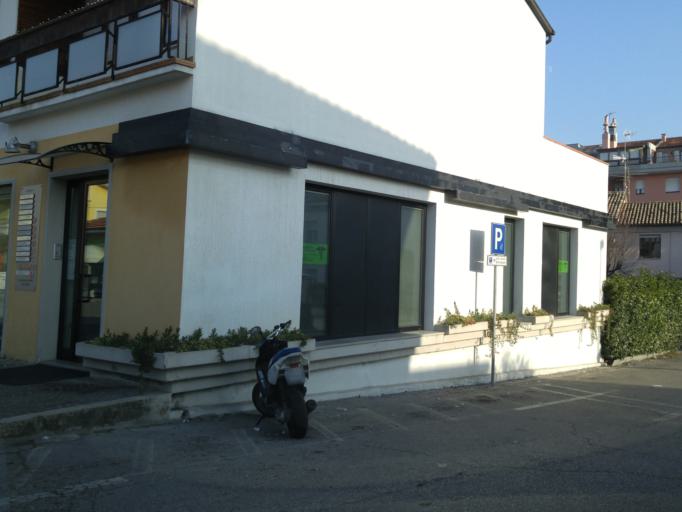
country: IT
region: The Marches
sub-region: Provincia di Pesaro e Urbino
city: Lucrezia
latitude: 43.7752
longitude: 12.9371
